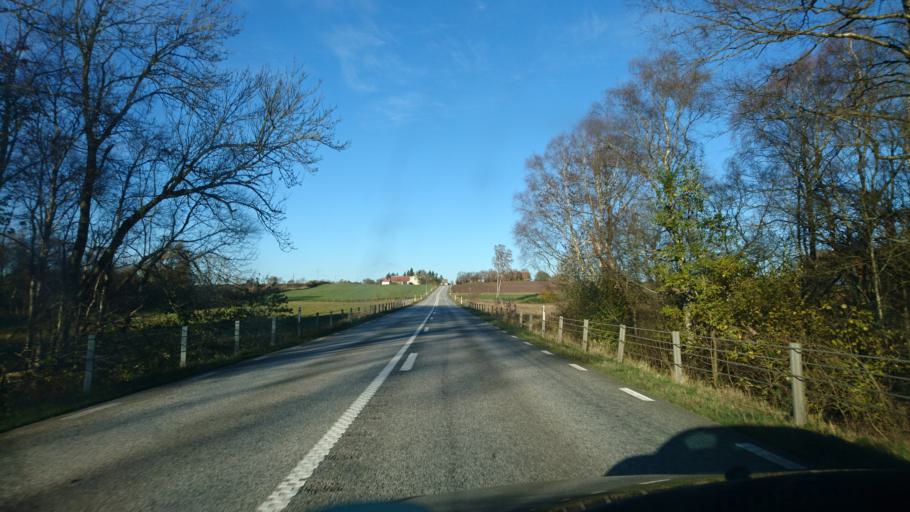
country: SE
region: Skane
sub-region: Tomelilla Kommun
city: Tomelilla
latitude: 55.6012
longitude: 13.9905
